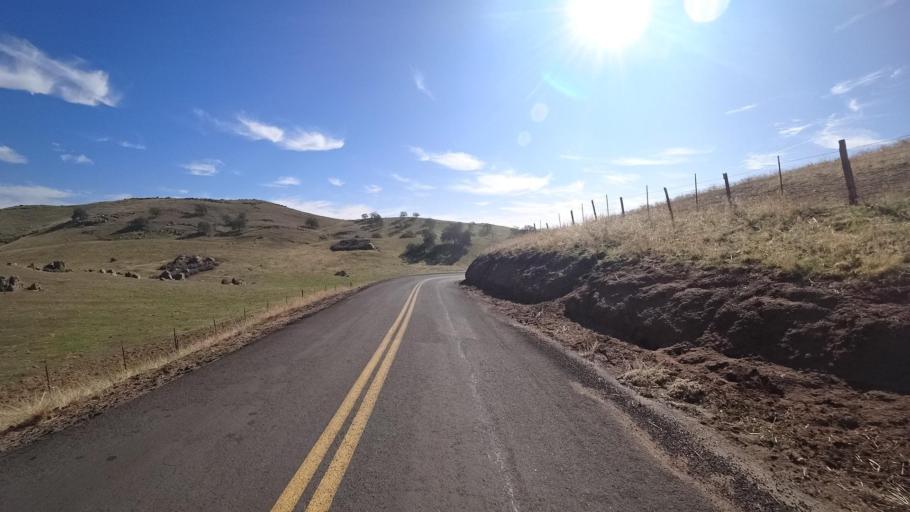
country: US
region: California
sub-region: Tulare County
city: Richgrove
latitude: 35.6859
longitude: -118.8801
